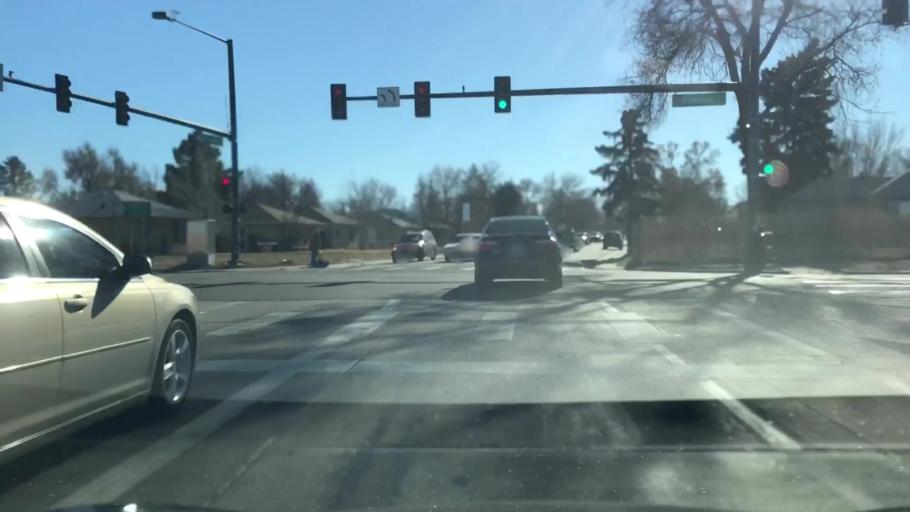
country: US
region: Colorado
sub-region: Adams County
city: Aurora
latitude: 39.7477
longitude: -104.8848
